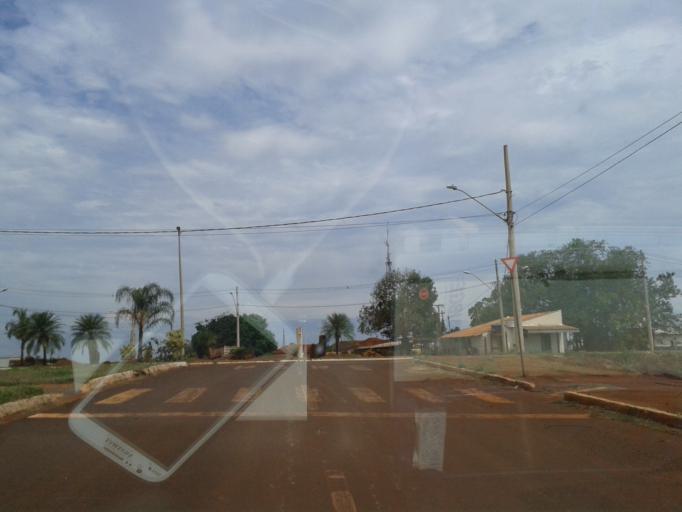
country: BR
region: Goias
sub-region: Itumbiara
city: Itumbiara
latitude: -18.4277
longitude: -49.1916
